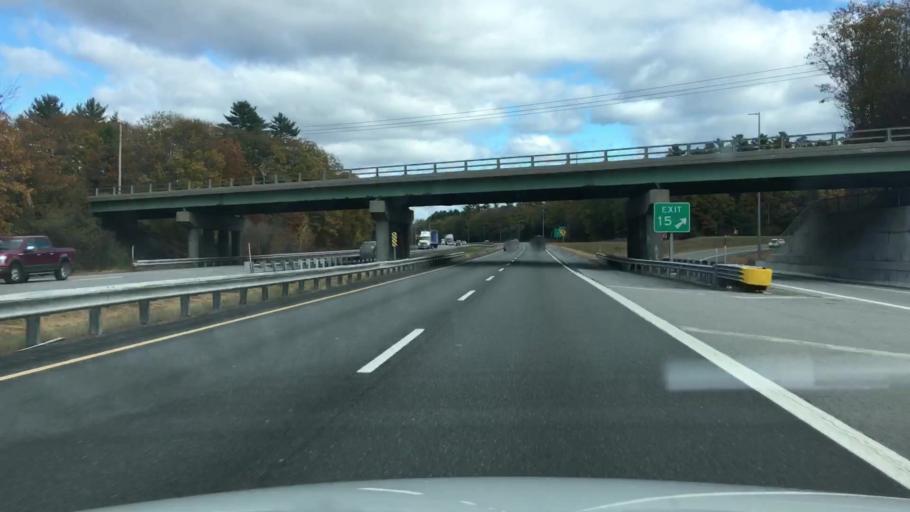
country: US
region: Maine
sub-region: Cumberland County
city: Yarmouth
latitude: 43.7844
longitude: -70.1908
